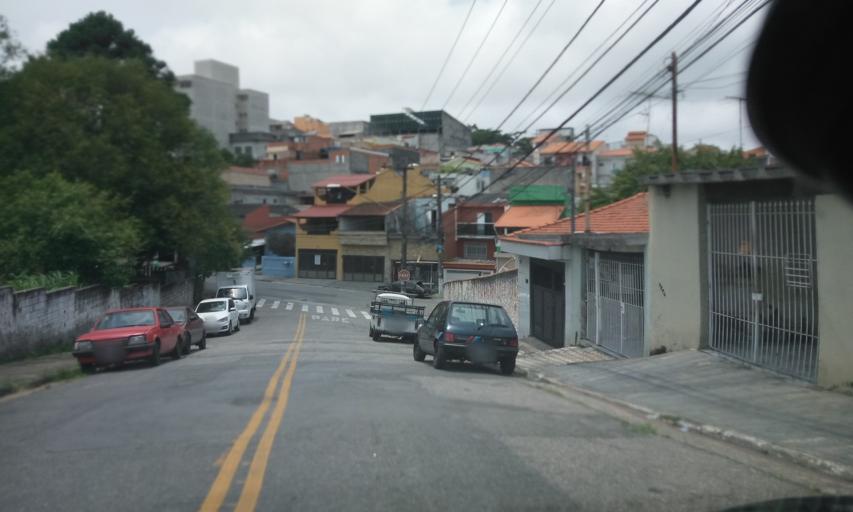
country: BR
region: Sao Paulo
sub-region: Sao Bernardo Do Campo
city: Sao Bernardo do Campo
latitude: -23.7015
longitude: -46.5717
